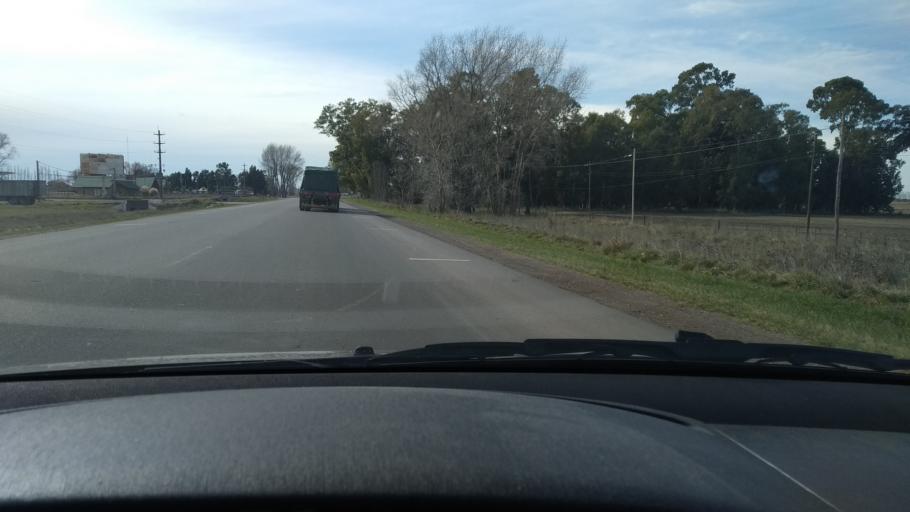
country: AR
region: Buenos Aires
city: Olavarria
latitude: -36.9483
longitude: -60.2446
